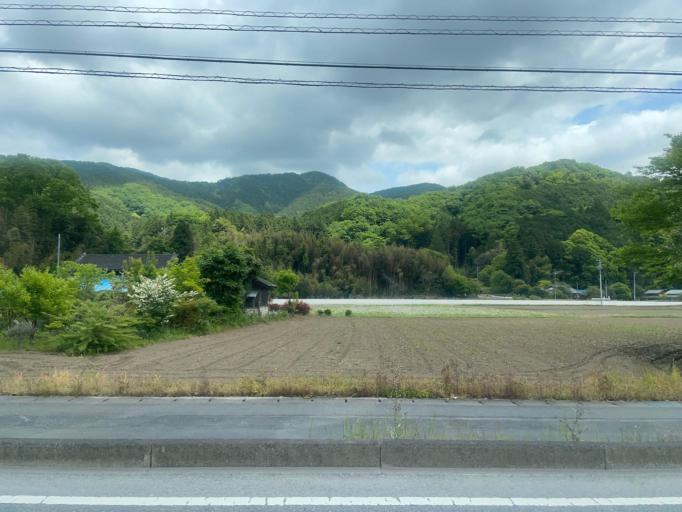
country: JP
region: Tochigi
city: Tanuma
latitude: 36.4683
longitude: 139.6332
